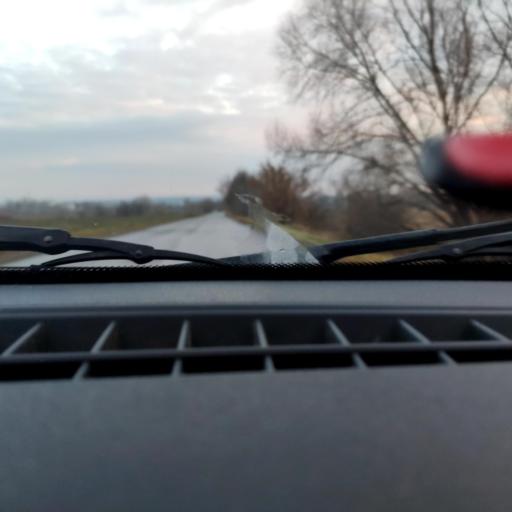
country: RU
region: Bashkortostan
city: Avdon
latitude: 54.5071
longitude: 55.8772
